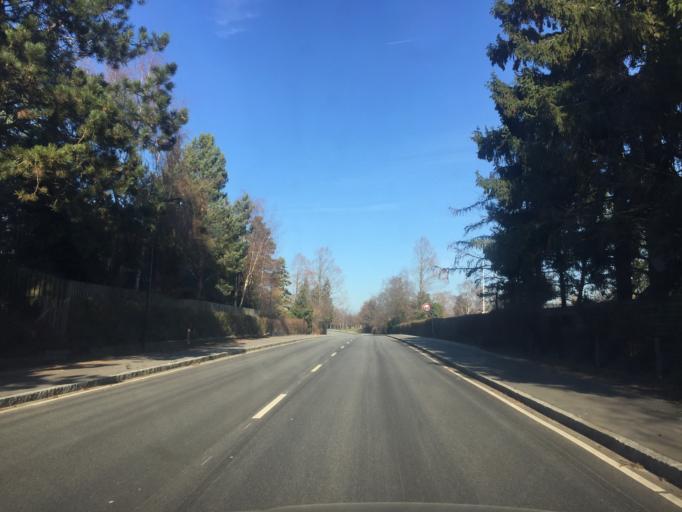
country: DK
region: Capital Region
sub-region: Rudersdal Kommune
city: Trorod
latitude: 55.8403
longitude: 12.5297
